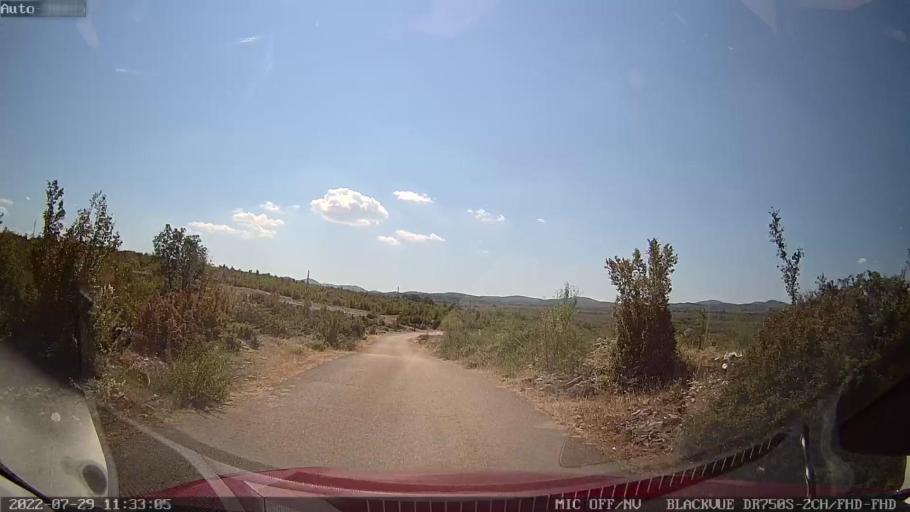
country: HR
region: Zadarska
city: Obrovac
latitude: 44.1888
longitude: 15.7323
